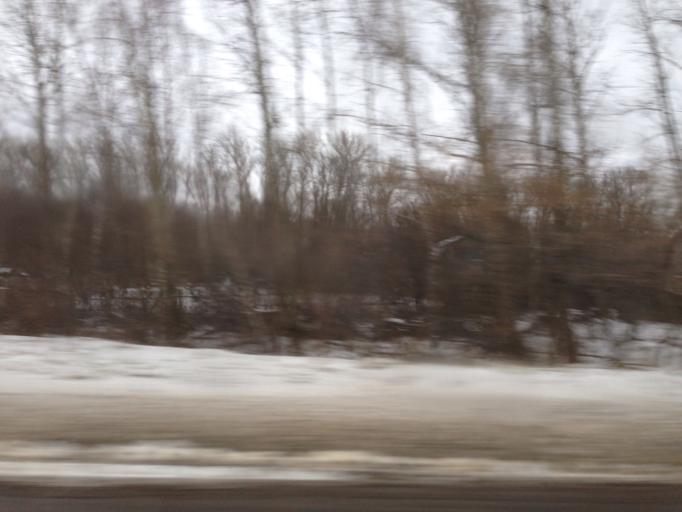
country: RU
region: Tula
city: Uzlovaya
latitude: 54.0045
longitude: 38.1704
